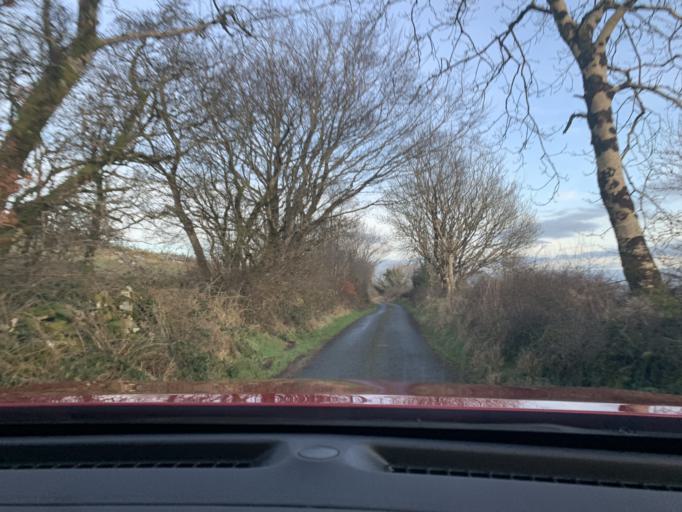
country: IE
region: Connaught
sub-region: Sligo
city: Strandhill
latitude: 54.1767
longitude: -8.6483
